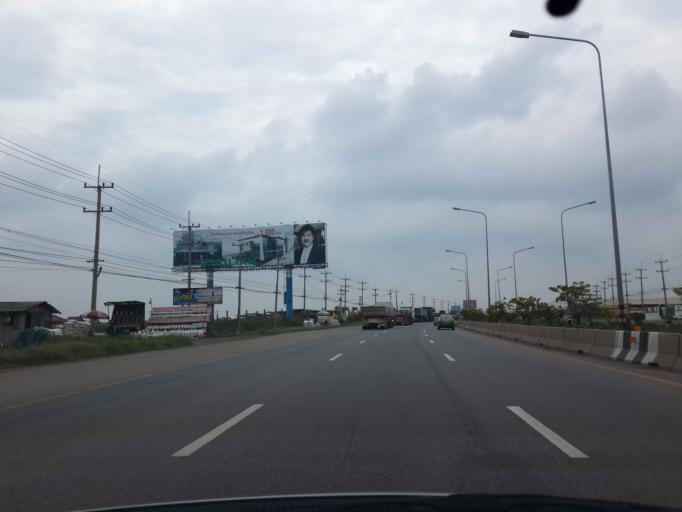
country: TH
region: Samut Sakhon
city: Ban Phaeo
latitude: 13.4739
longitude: 100.1156
